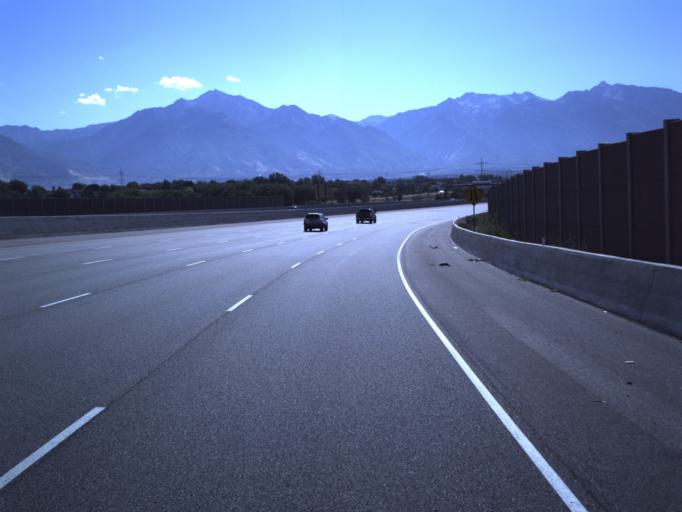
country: US
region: Utah
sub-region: Salt Lake County
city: Taylorsville
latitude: 40.6439
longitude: -111.9292
